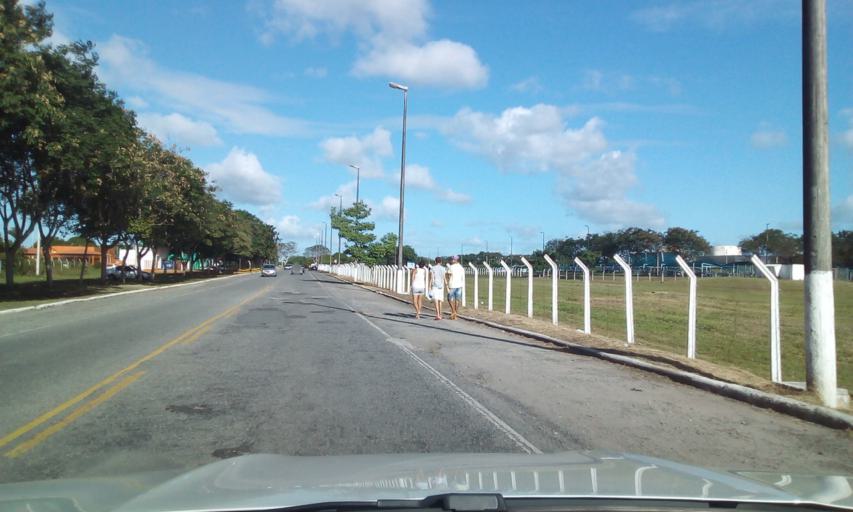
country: BR
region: Paraiba
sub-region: Bayeux
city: Bayeux
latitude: -7.1424
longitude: -34.9492
